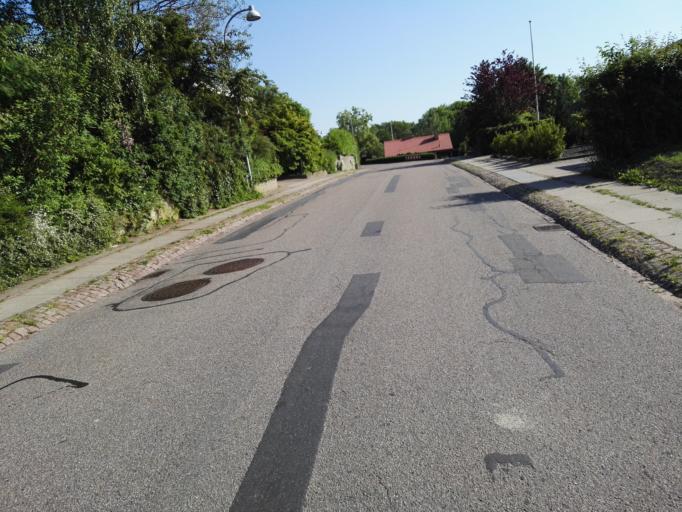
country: DK
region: Capital Region
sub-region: Ballerup Kommune
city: Malov
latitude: 55.7540
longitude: 12.3173
